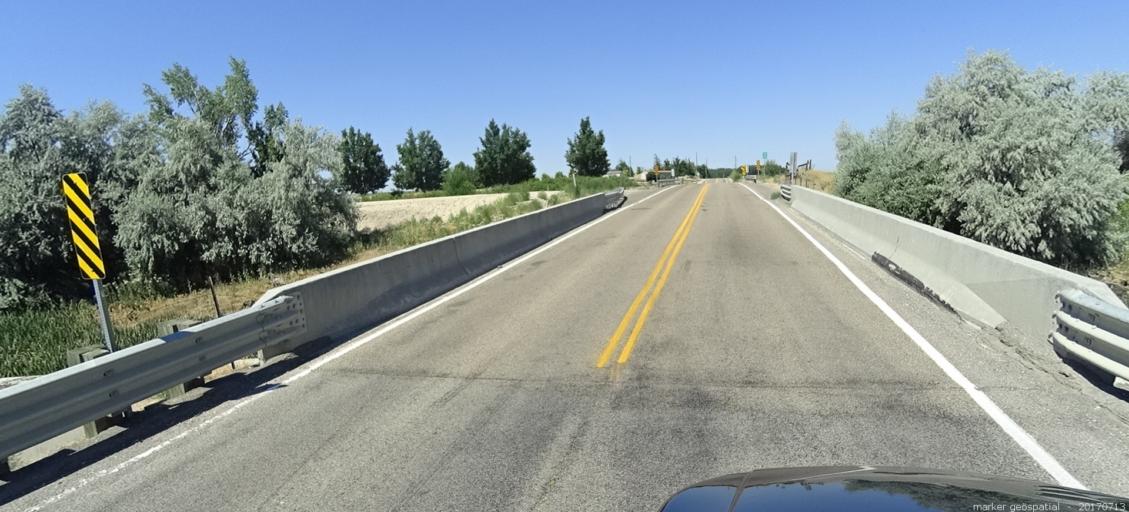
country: US
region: Idaho
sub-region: Ada County
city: Kuna
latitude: 43.5329
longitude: -116.4733
